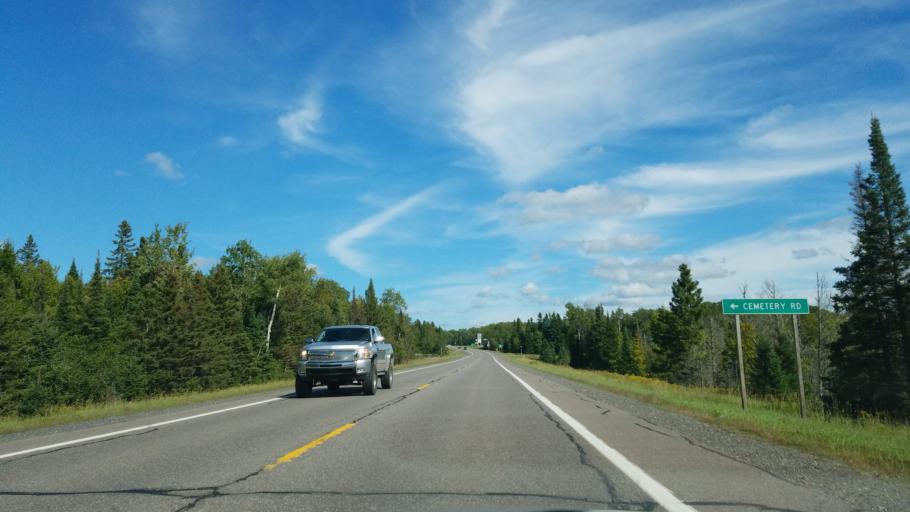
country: US
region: Michigan
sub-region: Baraga County
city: L'Anse
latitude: 46.5456
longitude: -88.5464
